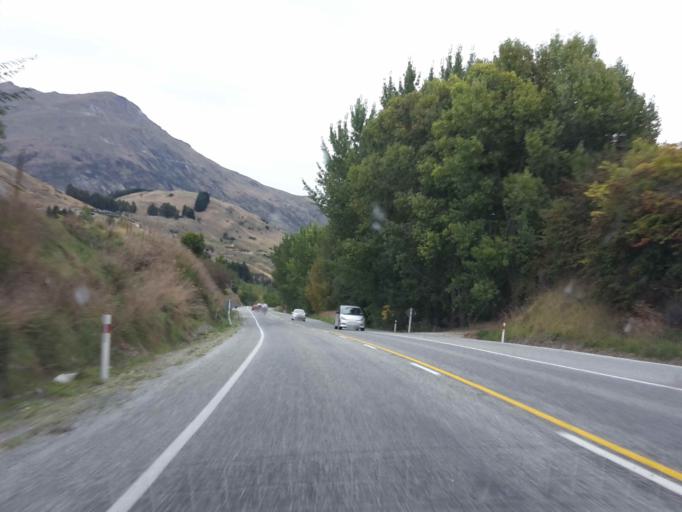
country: NZ
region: Otago
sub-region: Queenstown-Lakes District
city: Arrowtown
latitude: -44.9809
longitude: 168.8236
